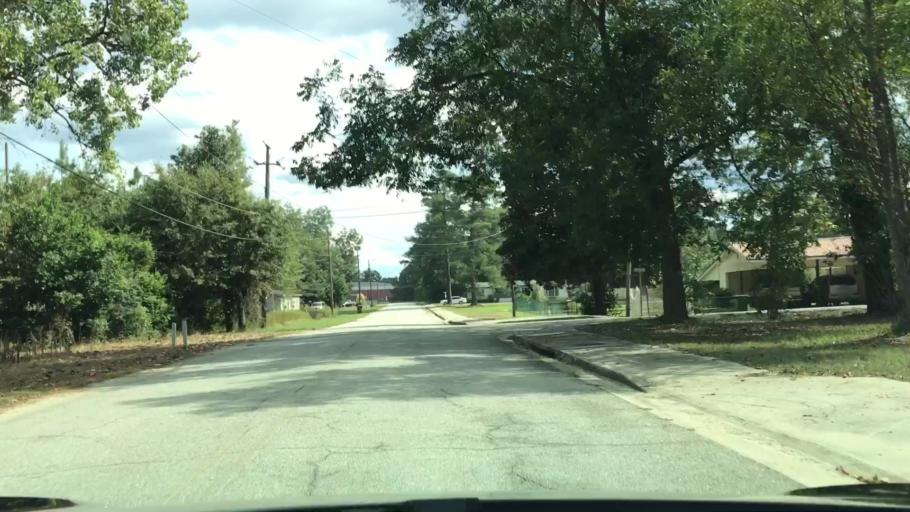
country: US
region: Georgia
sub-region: Jefferson County
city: Wadley
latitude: 32.8590
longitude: -82.3967
